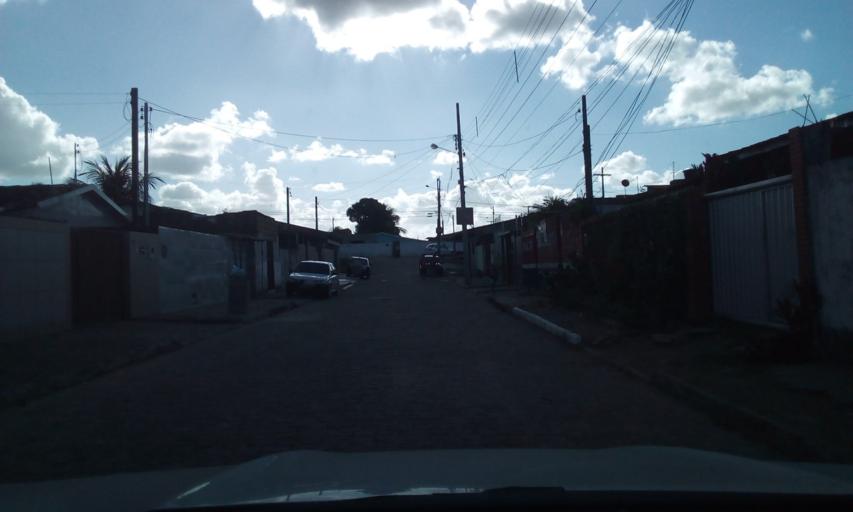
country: BR
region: Paraiba
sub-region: Bayeux
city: Bayeux
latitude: -7.1434
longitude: -34.9096
